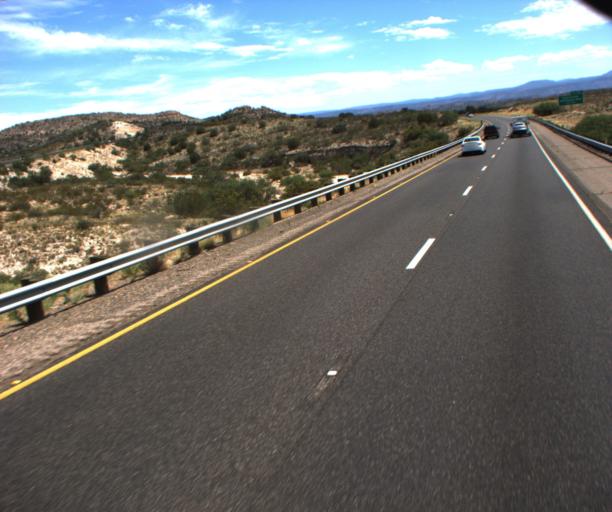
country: US
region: Arizona
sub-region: Yavapai County
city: Lake Montezuma
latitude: 34.6247
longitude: -111.8392
